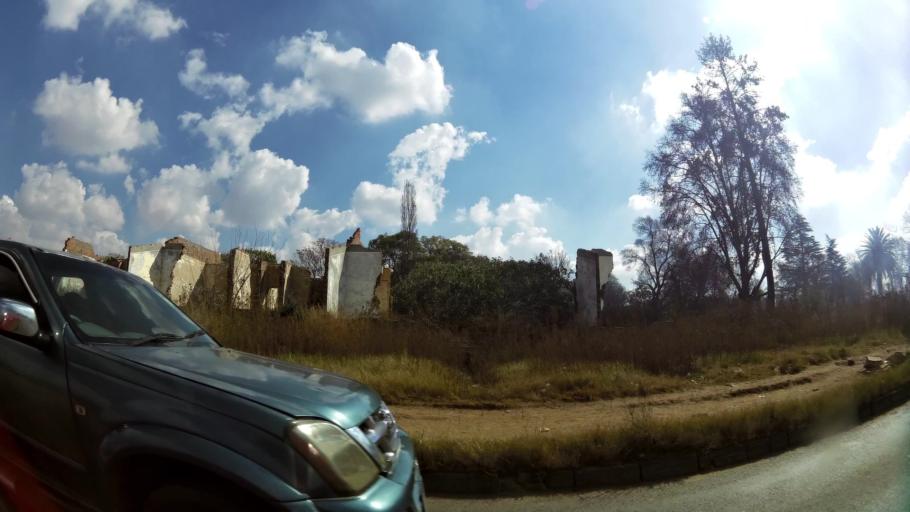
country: ZA
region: Gauteng
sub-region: City of Johannesburg Metropolitan Municipality
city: Roodepoort
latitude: -26.1750
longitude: 27.8729
